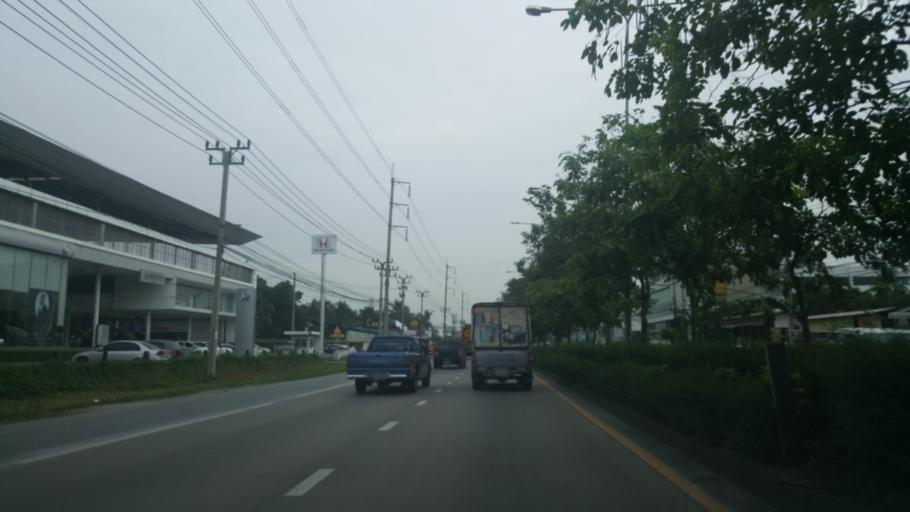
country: TH
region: Bangkok
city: Phasi Charoen
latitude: 13.6988
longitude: 100.4414
